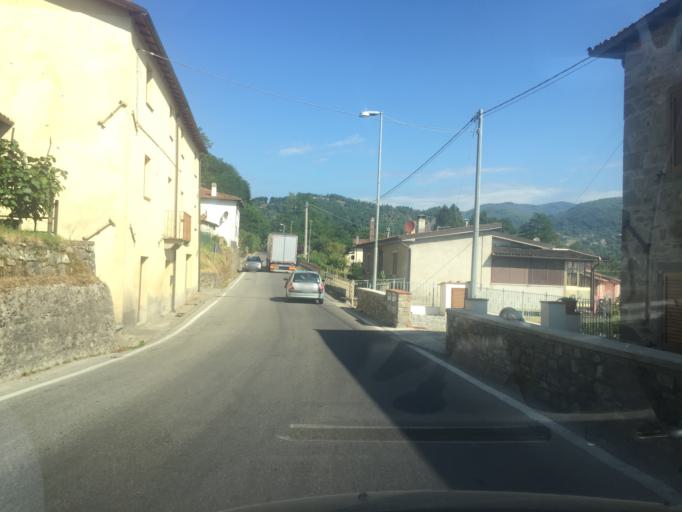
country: IT
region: Tuscany
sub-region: Provincia di Lucca
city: San Romano in Garfagnana
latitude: 44.1397
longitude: 10.3656
